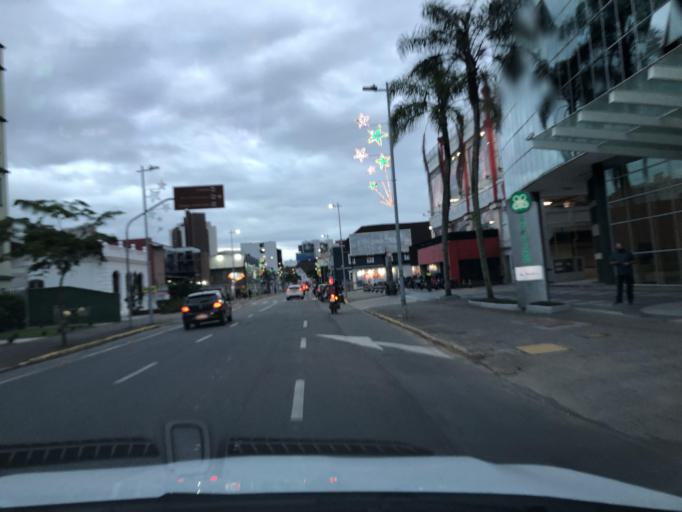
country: BR
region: Santa Catarina
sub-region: Joinville
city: Joinville
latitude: -26.3034
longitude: -48.8502
